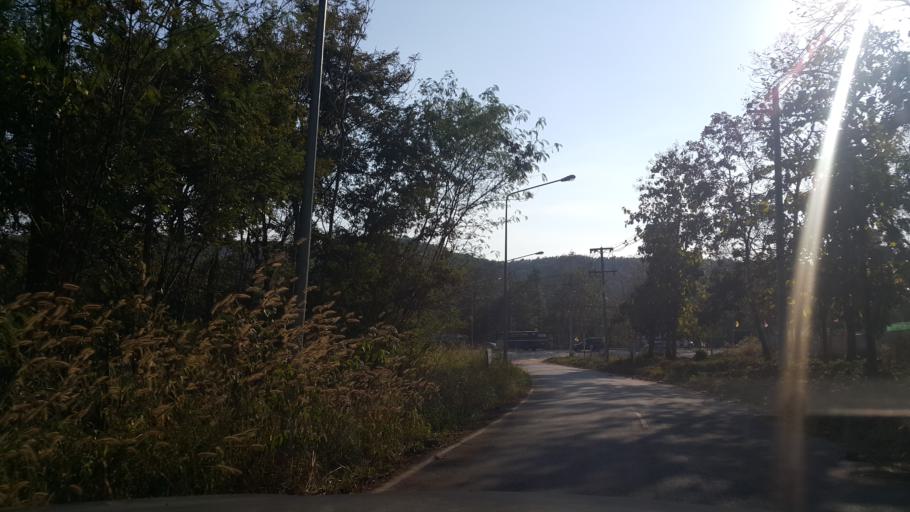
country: TH
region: Lamphun
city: Mae Tha
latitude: 18.5088
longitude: 99.1065
